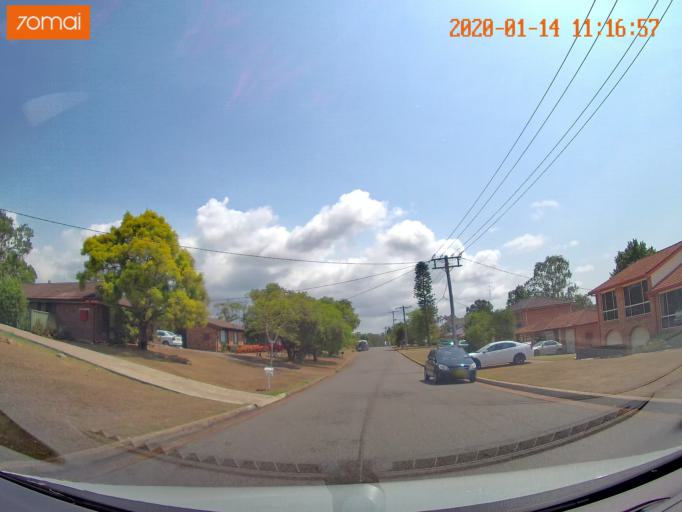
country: AU
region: New South Wales
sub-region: Lake Macquarie Shire
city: Cooranbong
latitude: -33.0966
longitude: 151.4616
